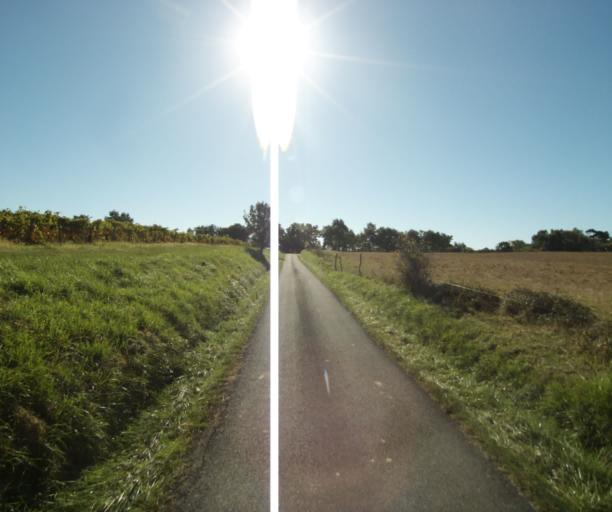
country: FR
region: Midi-Pyrenees
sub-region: Departement du Gers
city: Gondrin
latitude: 43.8128
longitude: 0.2021
